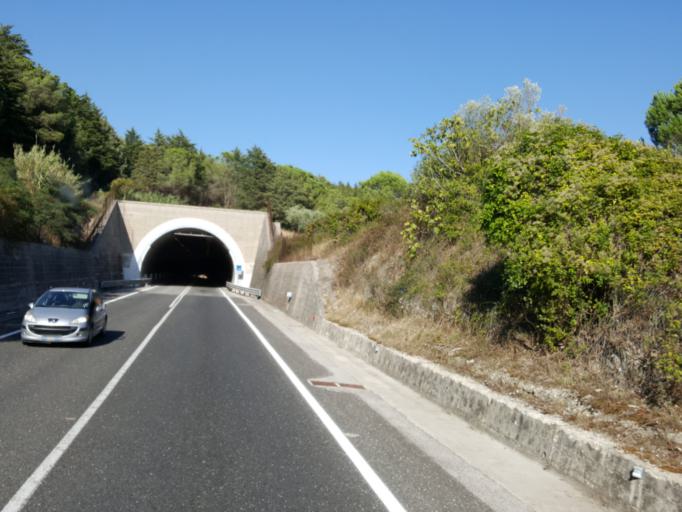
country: IT
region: Molise
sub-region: Provincia di Isernia
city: Macchia d'Isernia
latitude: 41.5520
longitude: 14.1633
